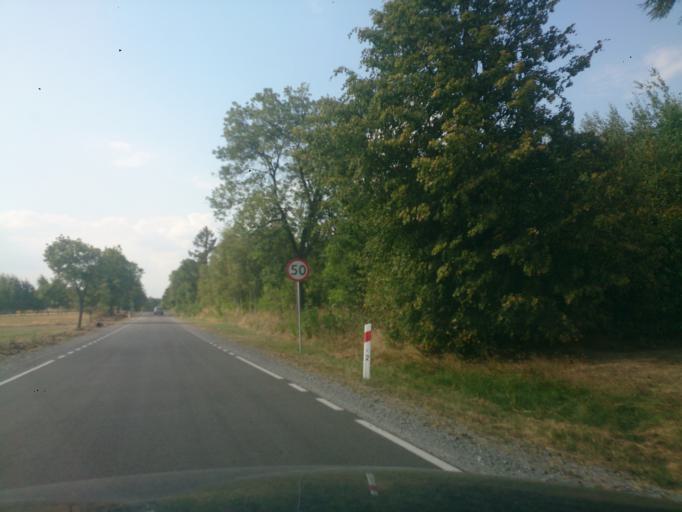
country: PL
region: Swietokrzyskie
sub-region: Powiat opatowski
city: Iwaniska
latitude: 50.6946
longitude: 21.3414
